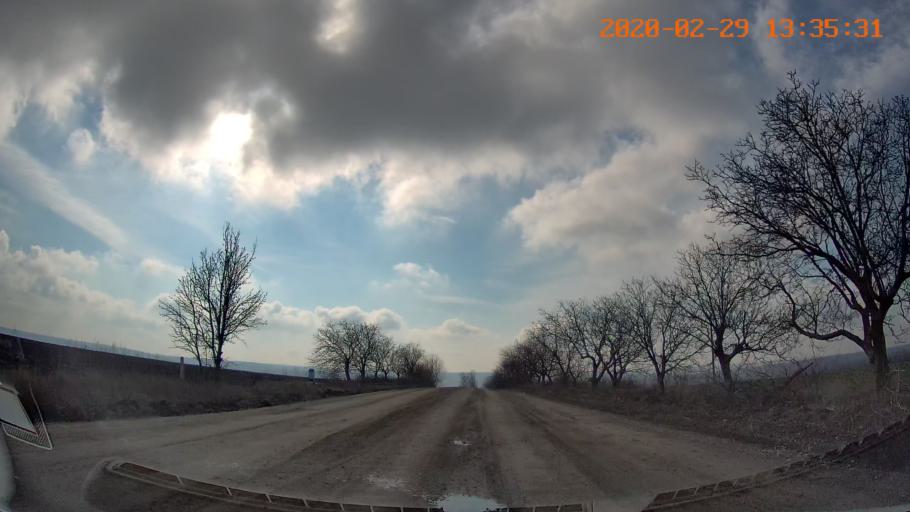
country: MD
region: Telenesti
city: Camenca
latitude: 47.8655
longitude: 28.6126
